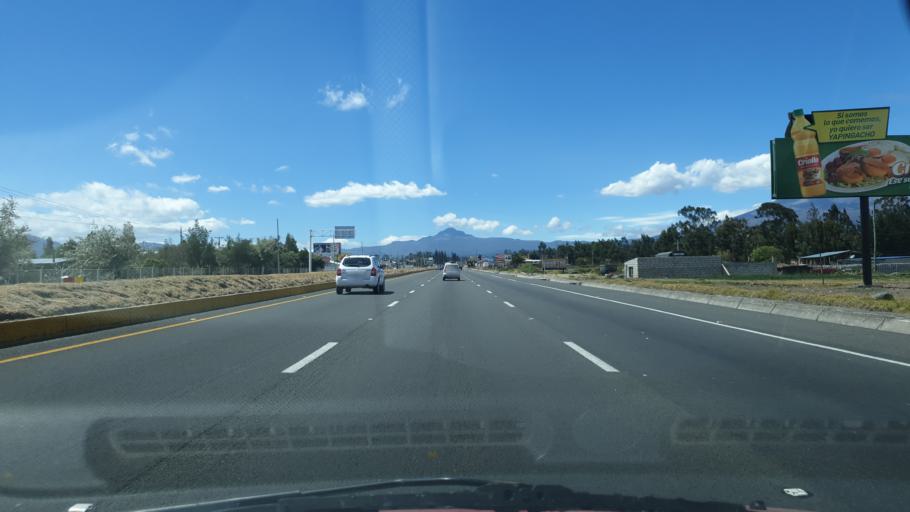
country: EC
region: Cotopaxi
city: Saquisili
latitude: -0.8108
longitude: -78.6243
